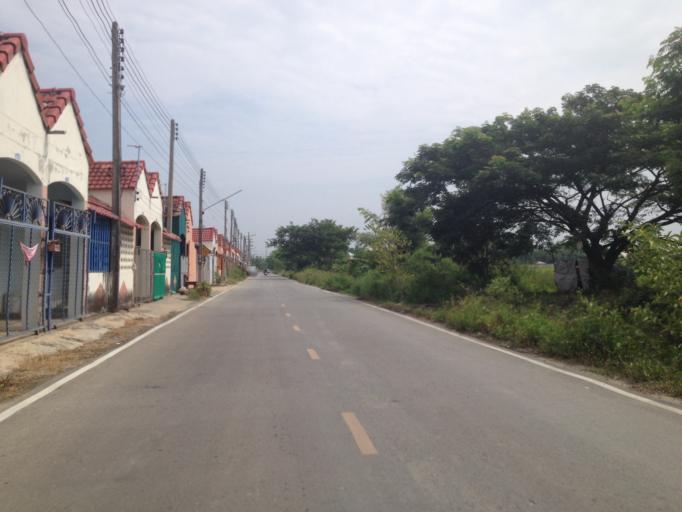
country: TH
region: Chiang Mai
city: San Pa Tong
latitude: 18.6552
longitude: 98.9013
